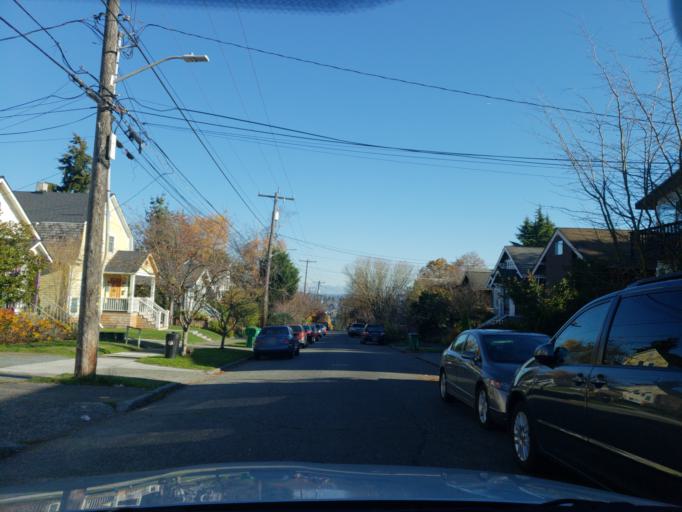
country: US
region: Washington
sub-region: King County
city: Seattle
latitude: 47.6739
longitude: -122.3540
